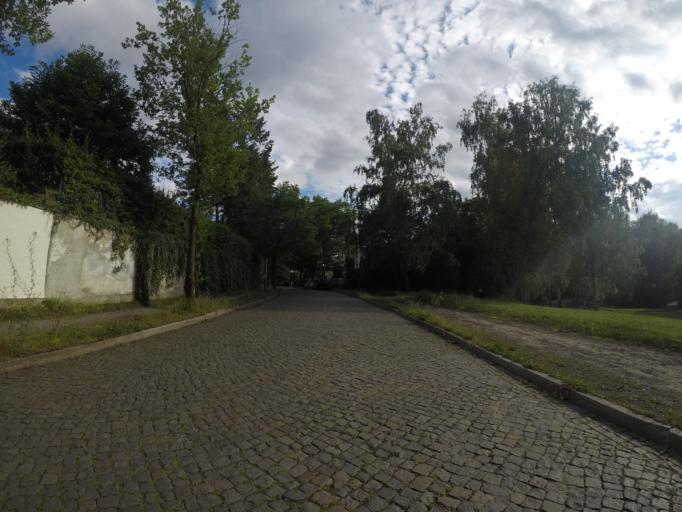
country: DE
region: Berlin
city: Dahlem
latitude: 52.4553
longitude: 13.2826
